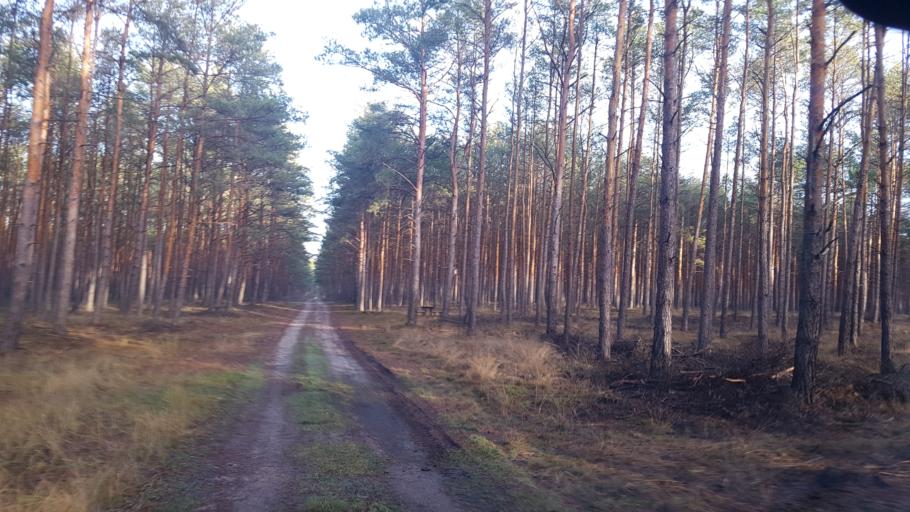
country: DE
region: Brandenburg
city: Schilda
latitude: 51.6249
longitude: 13.3923
